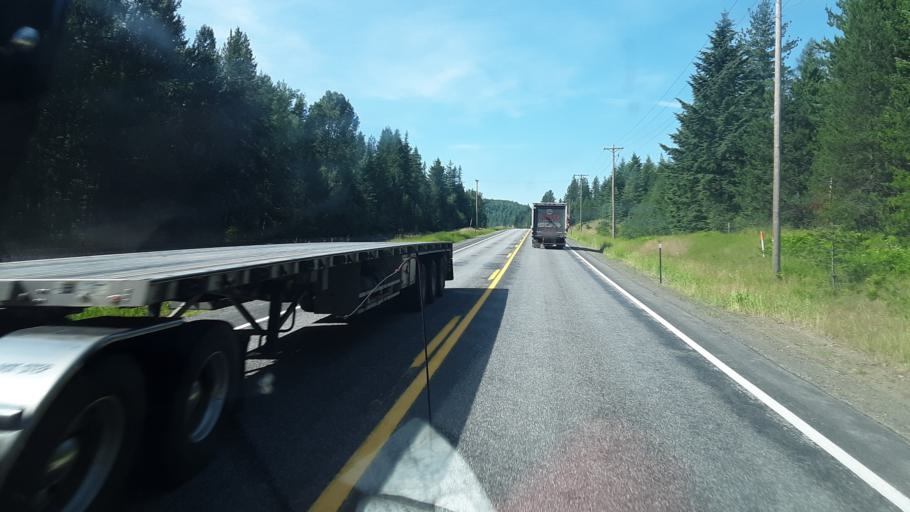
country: US
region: Idaho
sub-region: Bonner County
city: Ponderay
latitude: 48.4379
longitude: -116.4884
